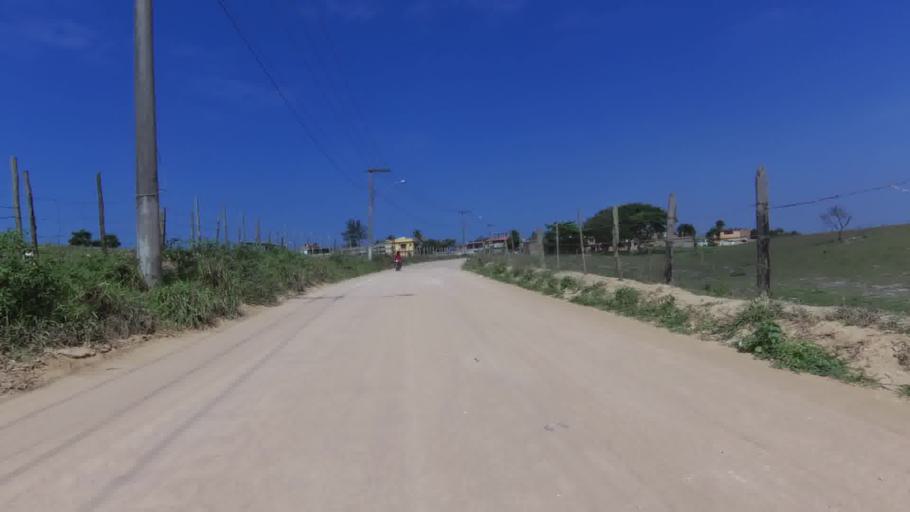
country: BR
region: Espirito Santo
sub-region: Marataizes
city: Marataizes
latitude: -21.0267
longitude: -40.8209
